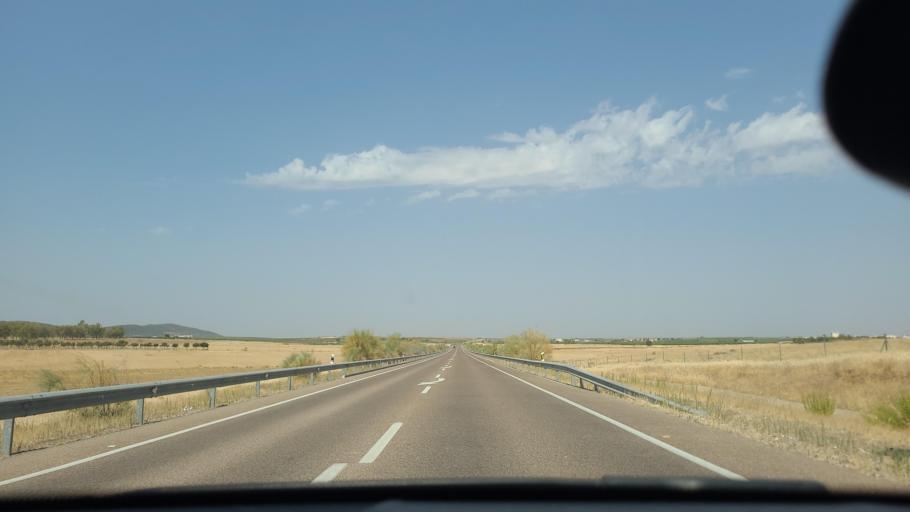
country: ES
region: Extremadura
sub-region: Provincia de Badajoz
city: Santa Marta
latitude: 38.5950
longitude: -6.6140
